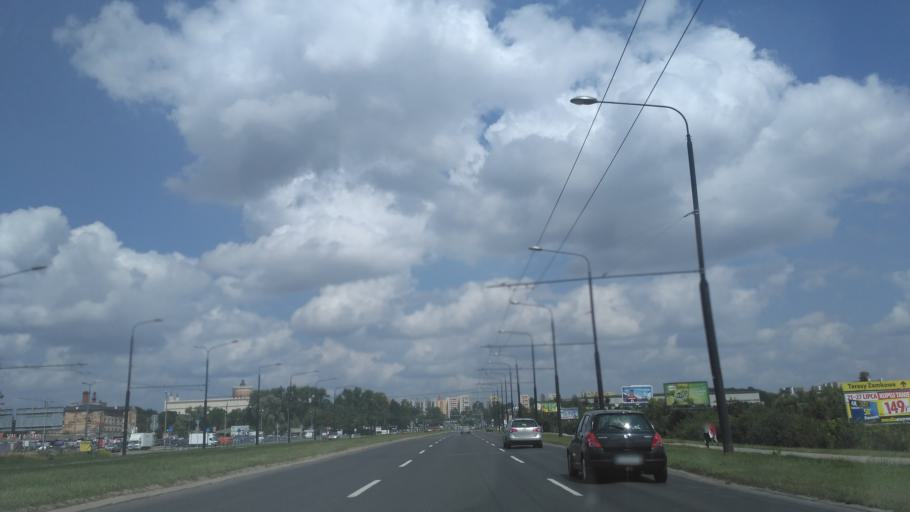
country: PL
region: Lublin Voivodeship
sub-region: Powiat lubelski
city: Lublin
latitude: 51.2442
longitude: 22.5736
